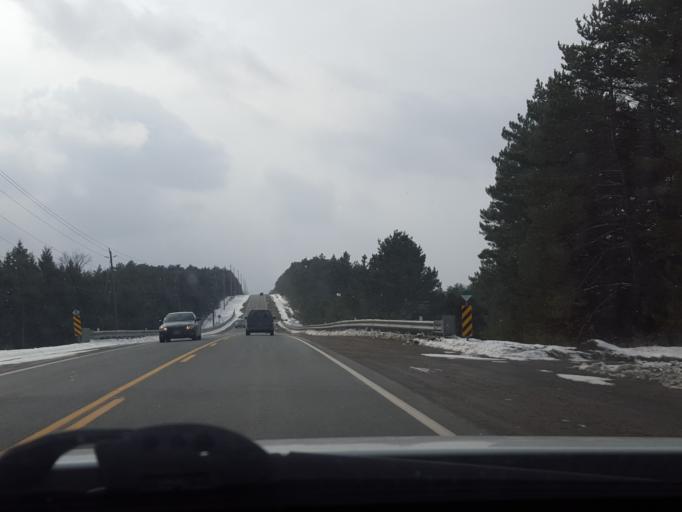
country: CA
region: Ontario
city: Uxbridge
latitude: 44.0494
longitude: -79.1310
